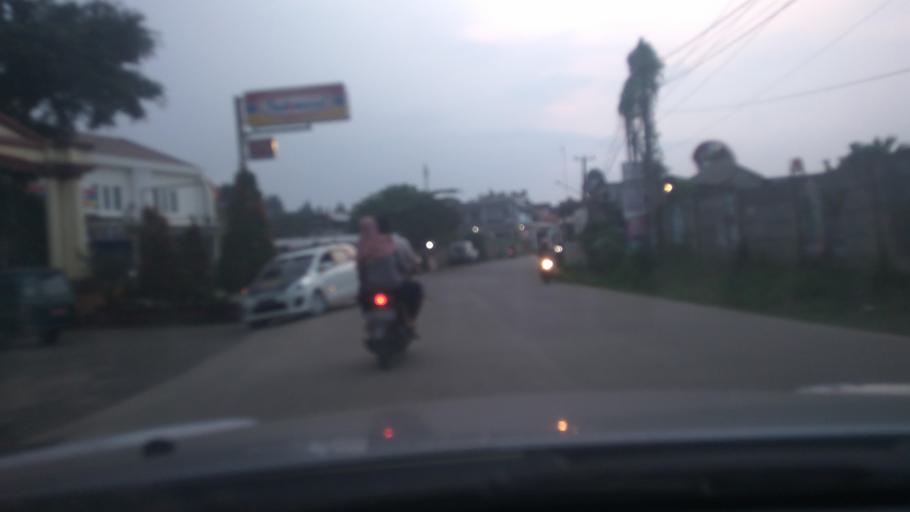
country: ID
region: West Java
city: Pamulang
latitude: -6.3689
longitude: 106.7426
